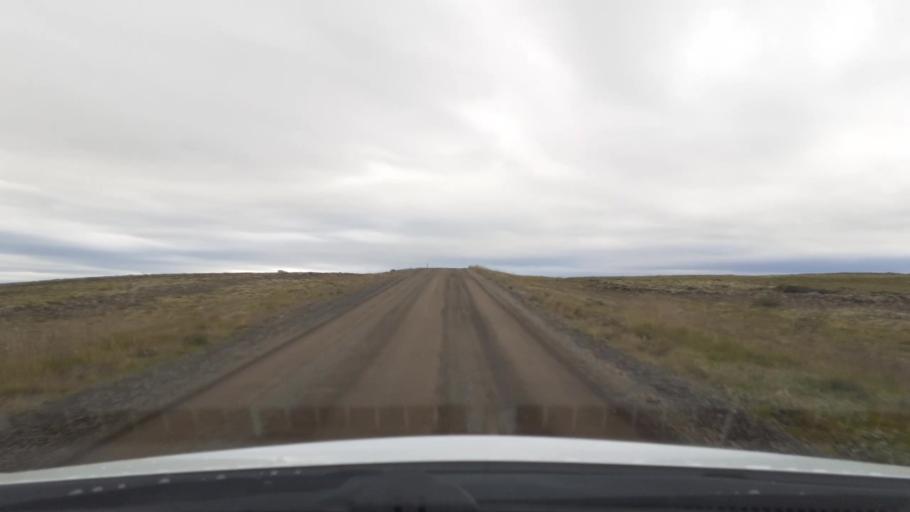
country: IS
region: Capital Region
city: Mosfellsbaer
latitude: 64.1969
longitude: -21.5530
